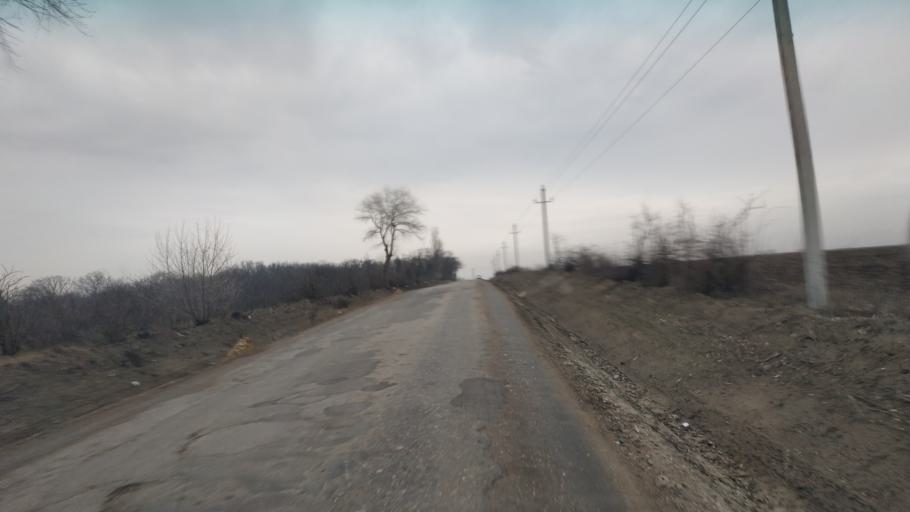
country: MD
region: Chisinau
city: Singera
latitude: 46.8522
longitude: 29.0083
